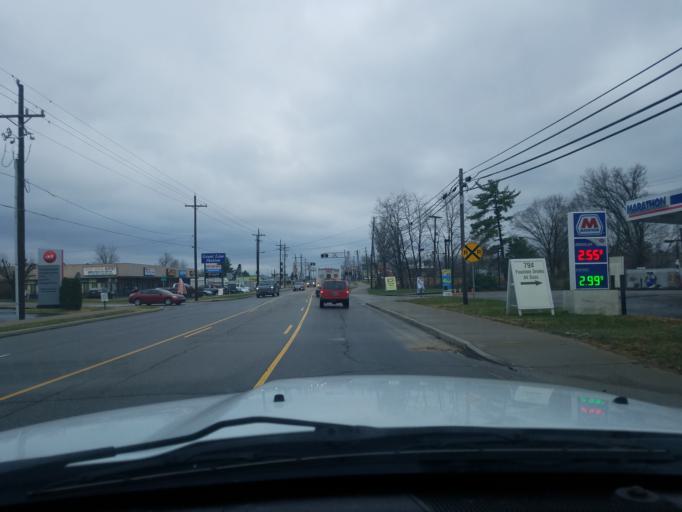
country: US
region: Indiana
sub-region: Floyd County
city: New Albany
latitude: 38.3274
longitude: -85.8191
